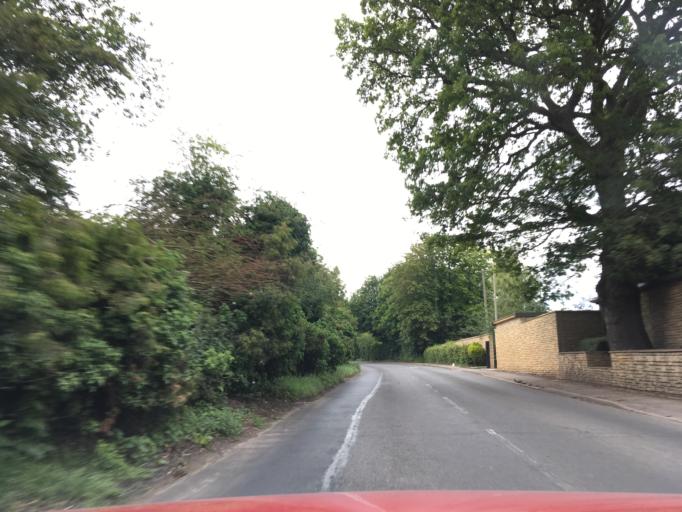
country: GB
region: England
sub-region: Oxfordshire
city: Boars Hill
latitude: 51.6999
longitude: -1.3034
